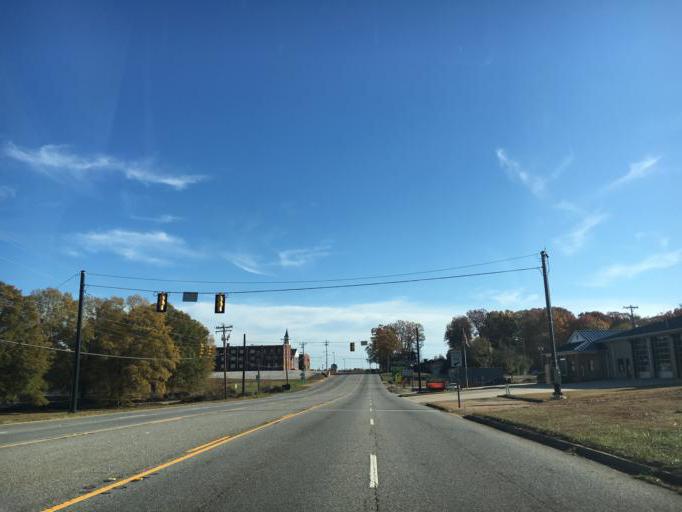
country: US
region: South Carolina
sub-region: Spartanburg County
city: Southern Shops
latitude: 35.0061
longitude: -82.0112
